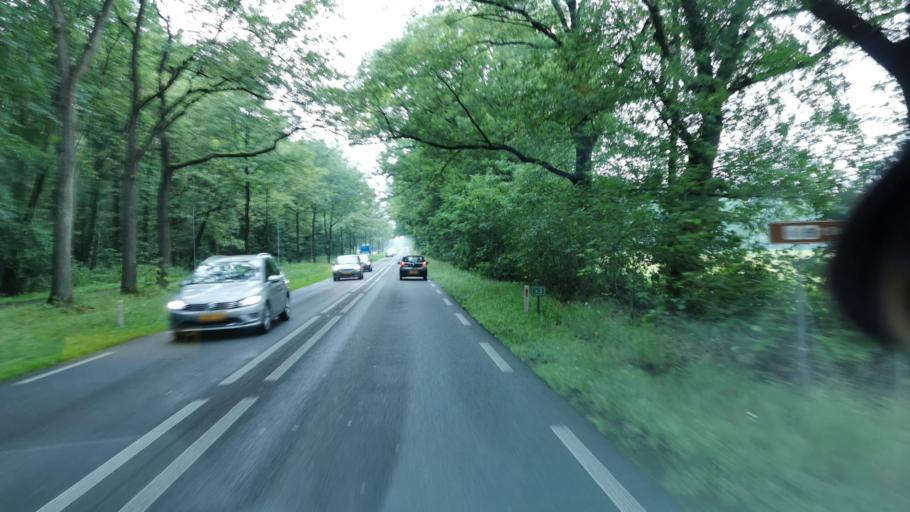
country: NL
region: Overijssel
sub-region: Gemeente Losser
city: Losser
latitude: 52.2773
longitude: 6.9741
